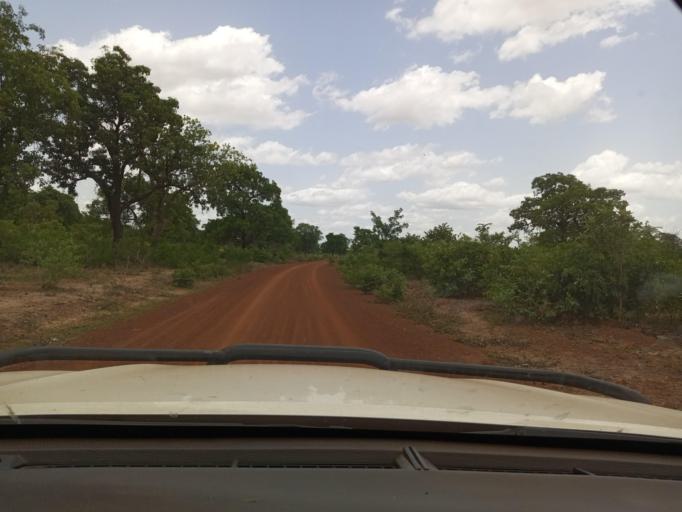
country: ML
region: Sikasso
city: Kolondieba
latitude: 11.7472
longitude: -6.7510
